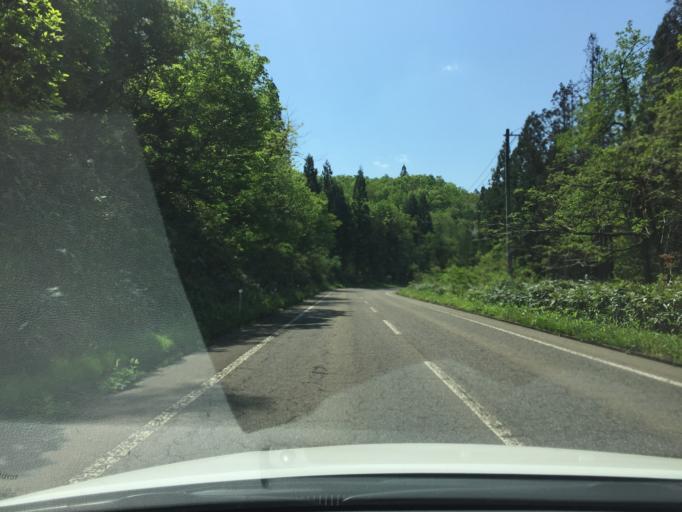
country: JP
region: Niigata
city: Tochio-honcho
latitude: 37.5363
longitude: 139.0924
